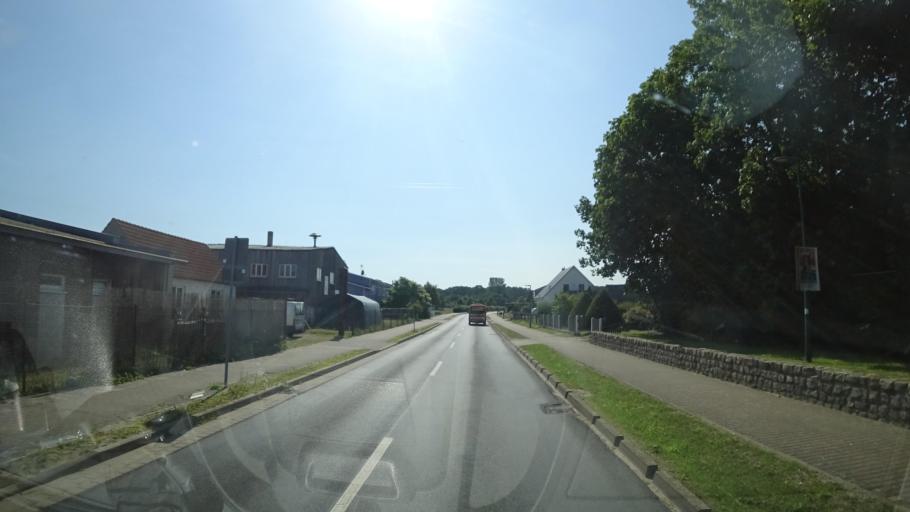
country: DE
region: Mecklenburg-Vorpommern
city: Kroslin
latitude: 54.1360
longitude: 13.7290
